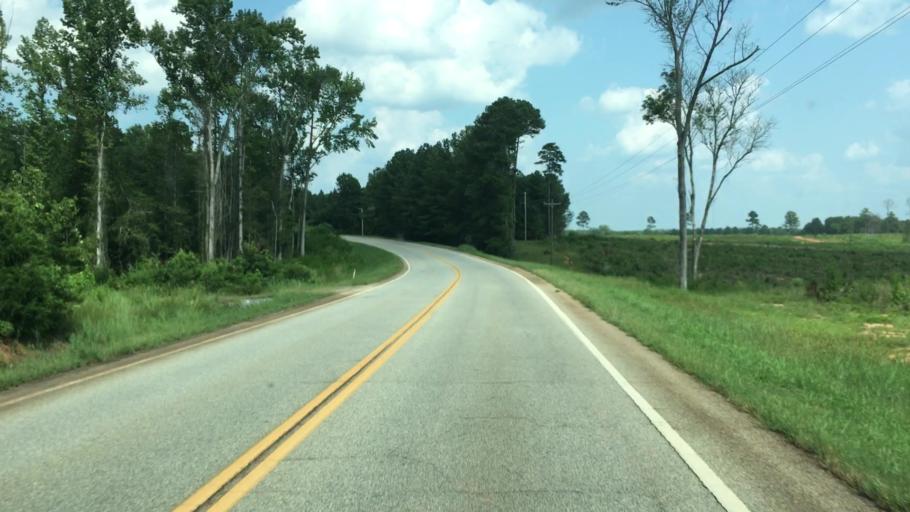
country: US
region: Georgia
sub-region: Monroe County
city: Forsyth
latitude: 33.1028
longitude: -83.8801
